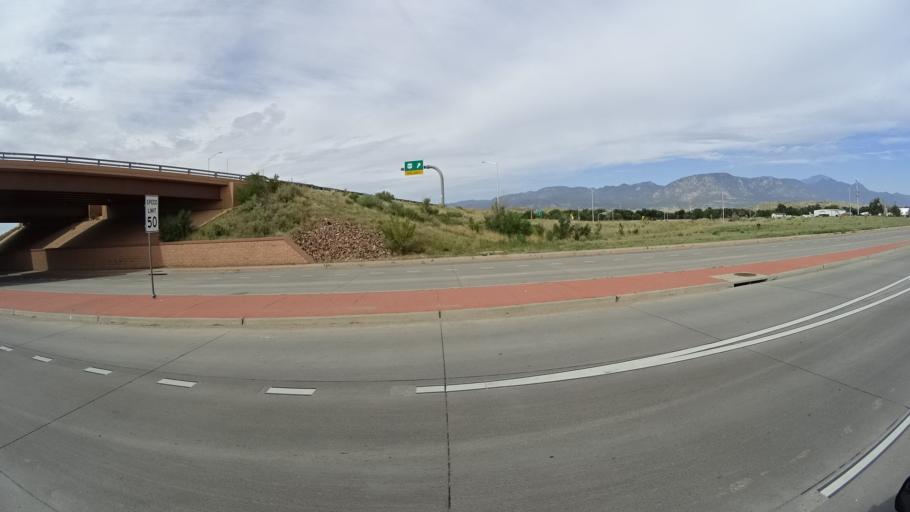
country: US
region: Colorado
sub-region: El Paso County
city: Security-Widefield
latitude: 38.7234
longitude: -104.7186
